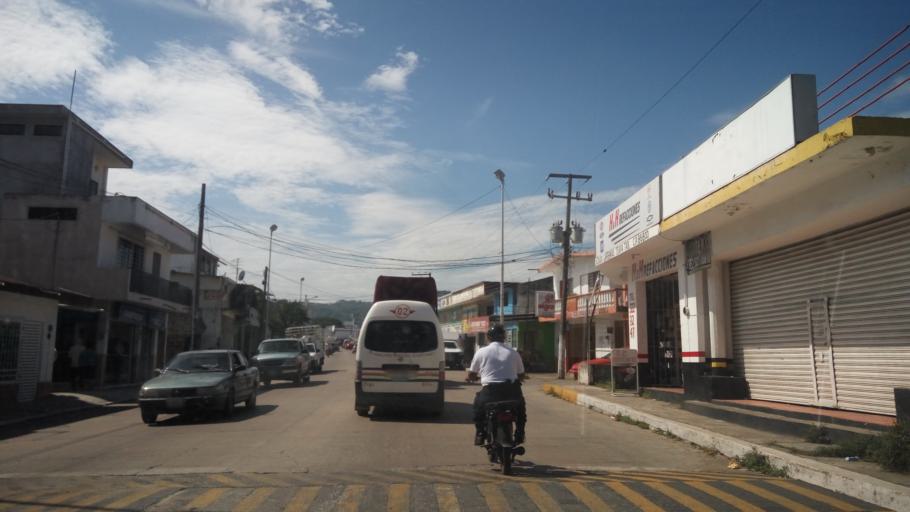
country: MX
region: Tabasco
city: Teapa
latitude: 17.5647
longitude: -92.9507
